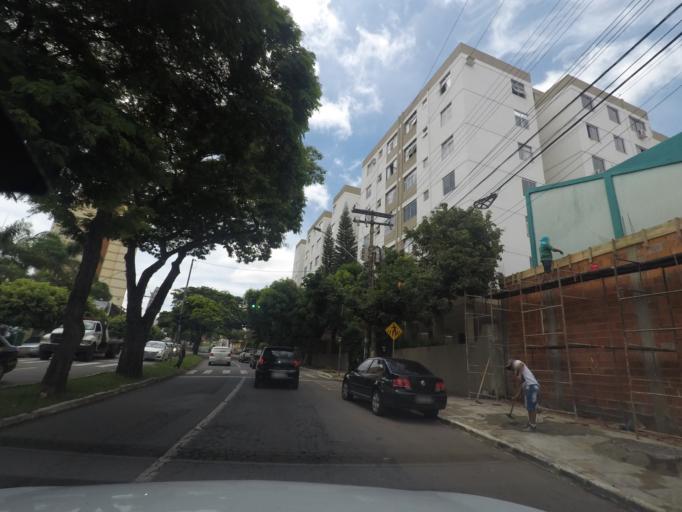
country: BR
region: Goias
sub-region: Goiania
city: Goiania
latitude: -16.6697
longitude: -49.2363
